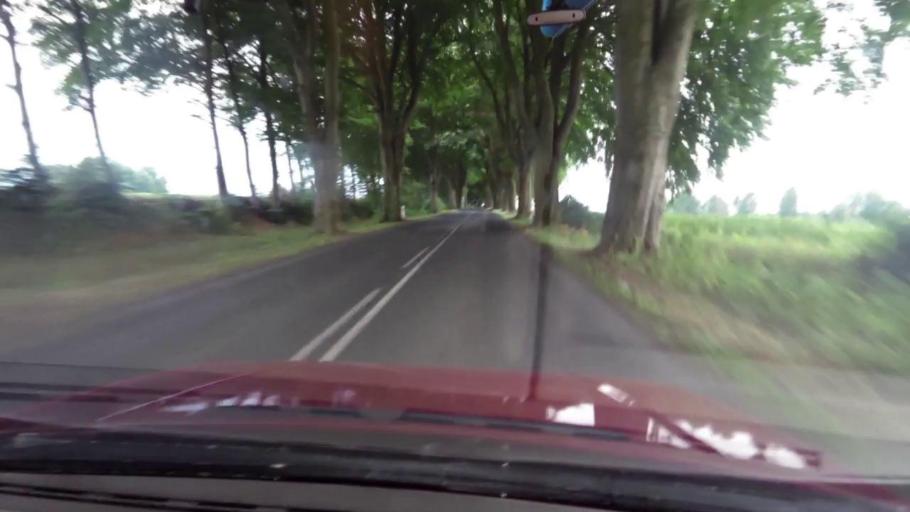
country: PL
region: West Pomeranian Voivodeship
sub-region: Powiat koszalinski
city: Polanow
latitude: 54.1415
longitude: 16.5421
